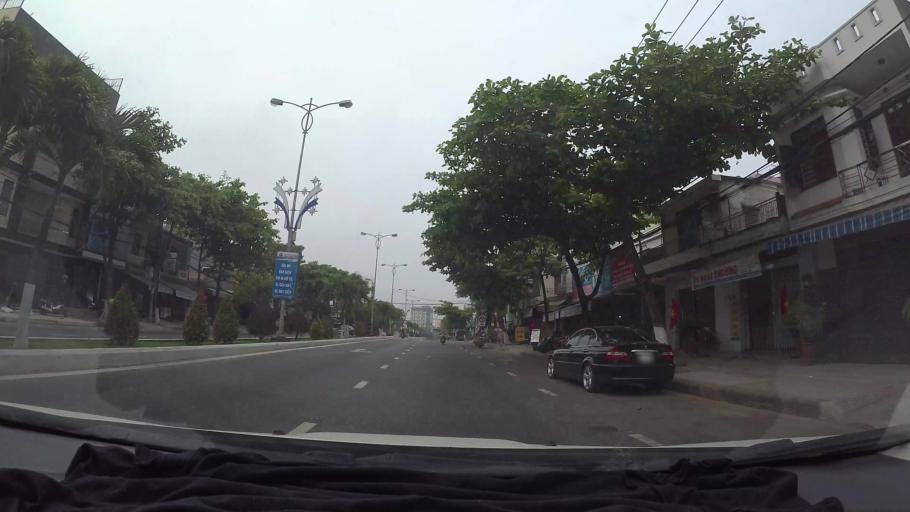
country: VN
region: Da Nang
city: Cam Le
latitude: 16.0217
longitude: 108.2129
